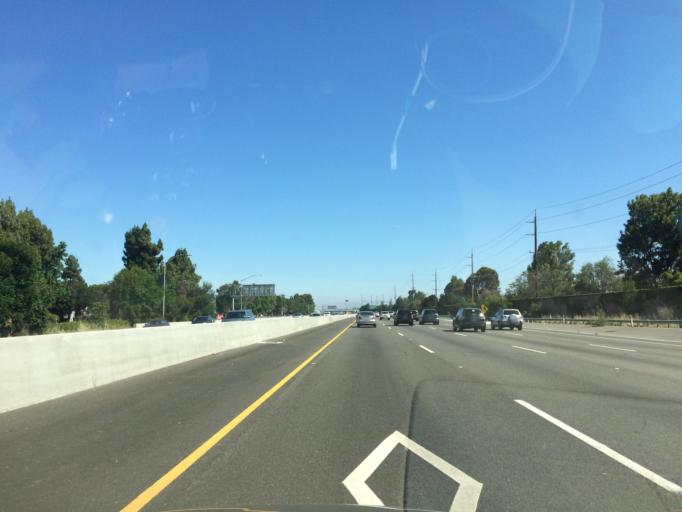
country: US
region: California
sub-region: Santa Clara County
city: Milpitas
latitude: 37.4039
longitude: -121.9095
